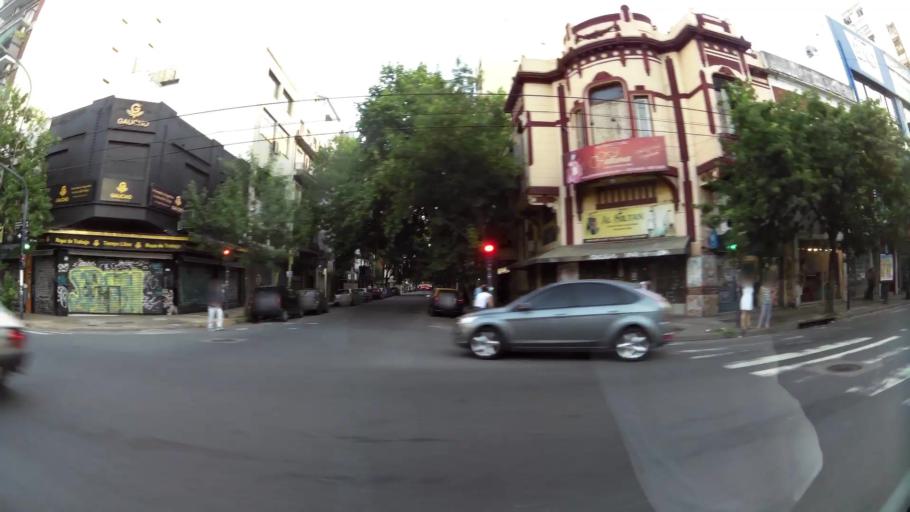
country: AR
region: Buenos Aires F.D.
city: Colegiales
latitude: -34.5992
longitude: -58.4378
